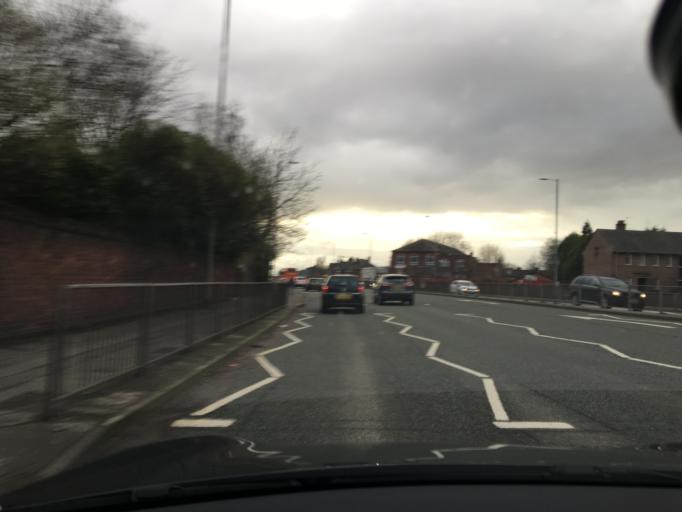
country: GB
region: England
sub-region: Manchester
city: Chorlton cum Hardy
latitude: 53.4235
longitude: -2.2573
